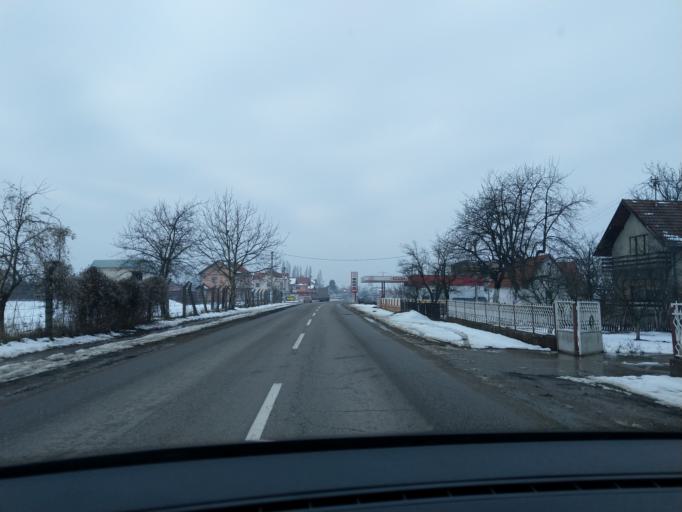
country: BA
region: Republika Srpska
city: Velika Obarska
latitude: 44.7978
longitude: 19.1736
